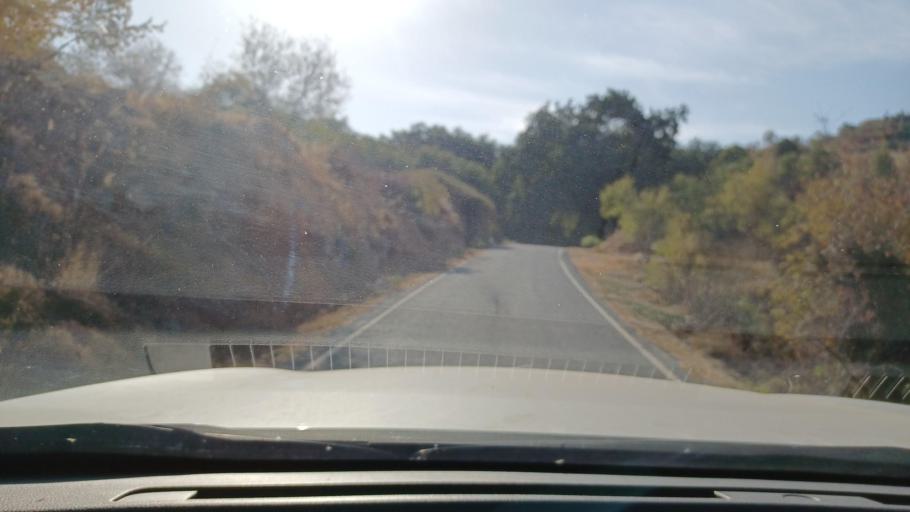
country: CY
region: Pafos
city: Polis
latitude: 35.0048
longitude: 32.5068
